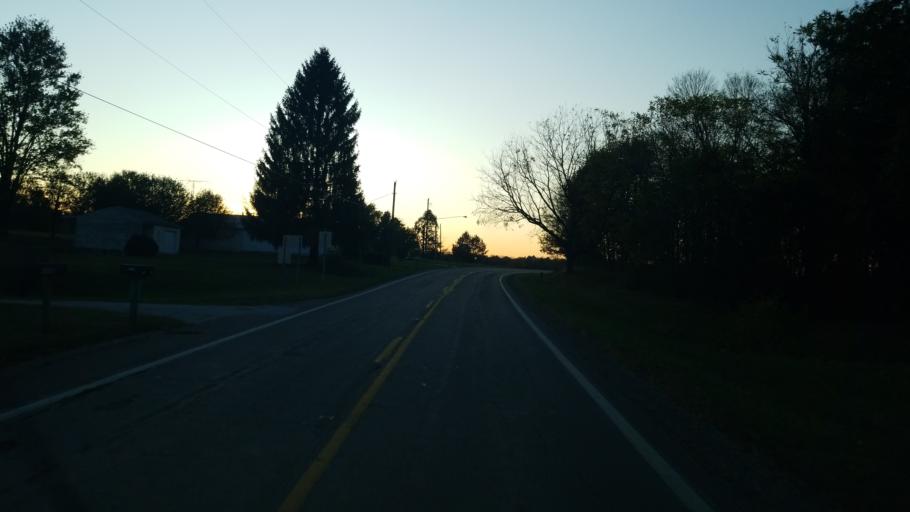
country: US
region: Ohio
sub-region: Morrow County
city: Cardington
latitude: 40.5063
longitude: -82.9033
